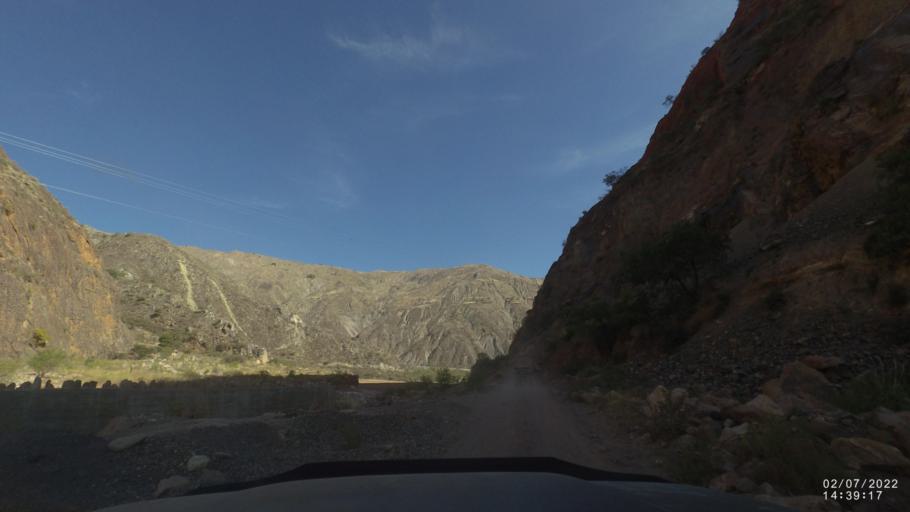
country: BO
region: Cochabamba
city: Irpa Irpa
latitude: -17.8467
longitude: -66.4190
